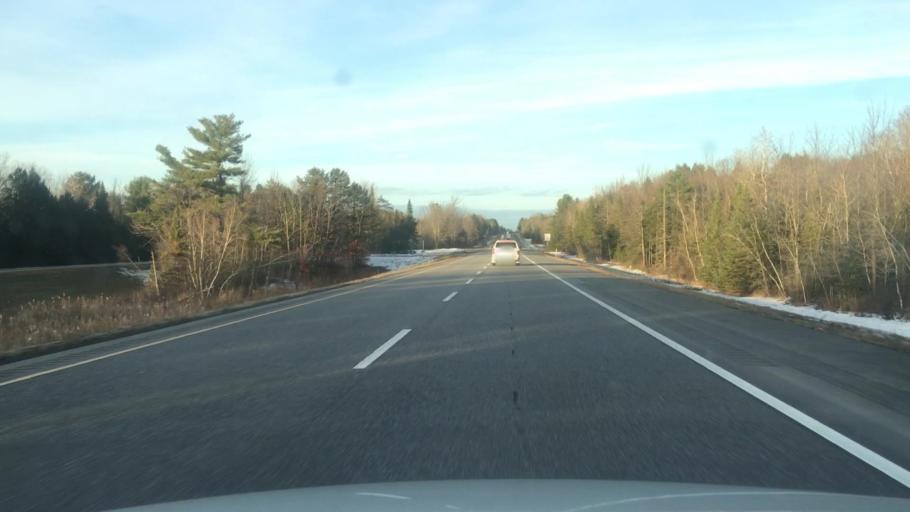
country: US
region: Maine
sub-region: Kennebec County
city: Sidney
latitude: 44.4095
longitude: -69.7475
